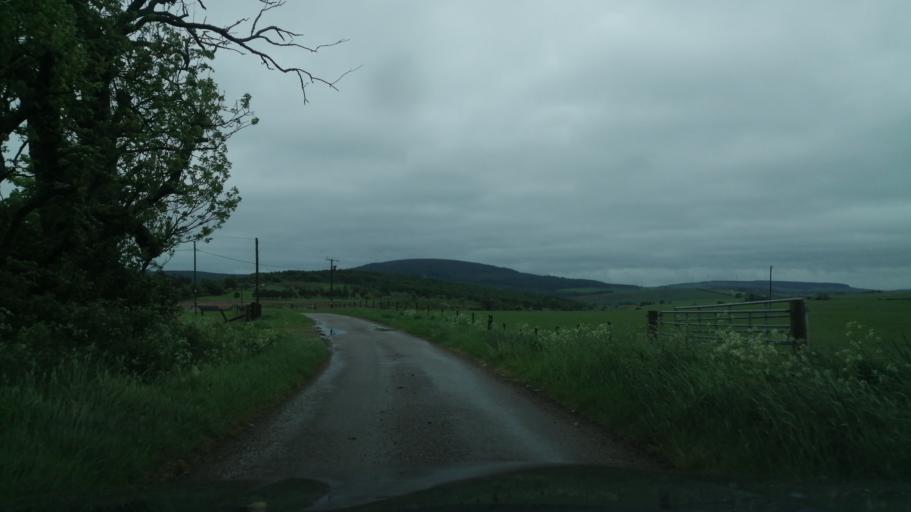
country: GB
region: Scotland
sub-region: Moray
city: Keith
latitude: 57.5718
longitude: -2.8613
